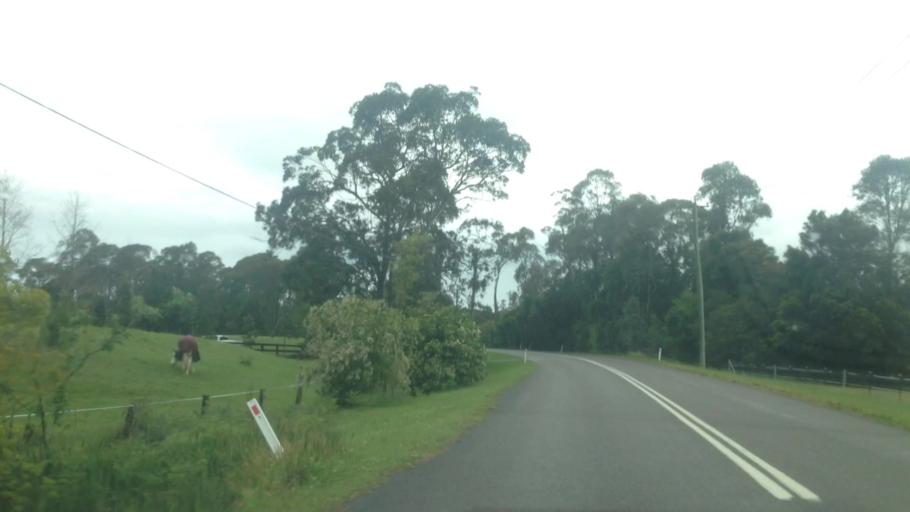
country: AU
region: New South Wales
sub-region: Wyong Shire
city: Little Jilliby
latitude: -33.2510
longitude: 151.3832
